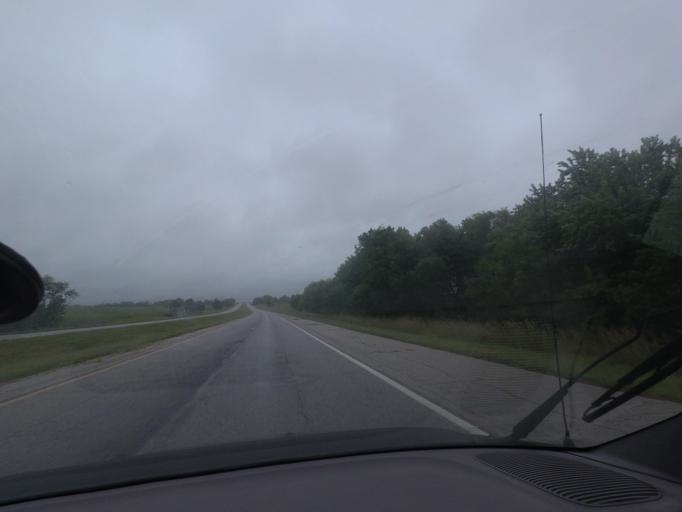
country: US
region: Illinois
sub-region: Pike County
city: Pittsfield
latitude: 39.6698
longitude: -90.8203
